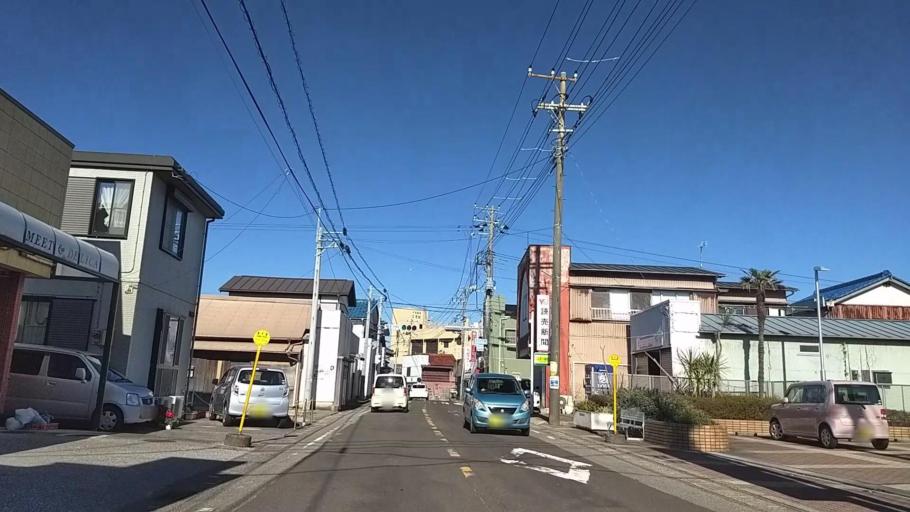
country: JP
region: Chiba
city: Tateyama
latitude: 34.9617
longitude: 139.9583
